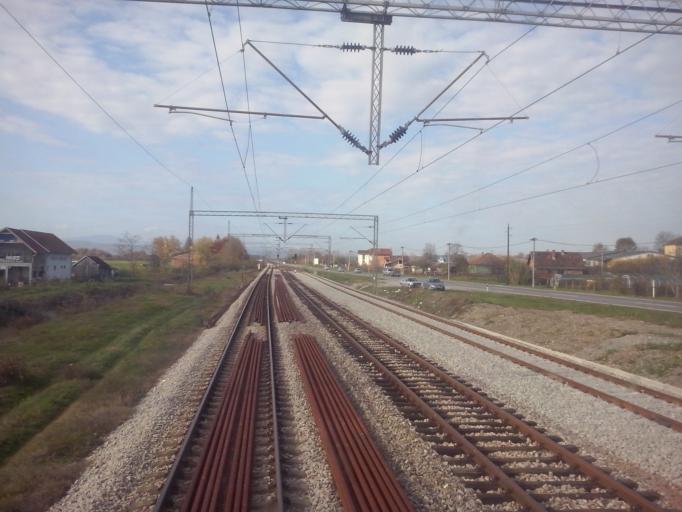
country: RS
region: Central Serbia
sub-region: Kolubarski Okrug
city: Mionica
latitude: 44.3001
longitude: 20.0264
